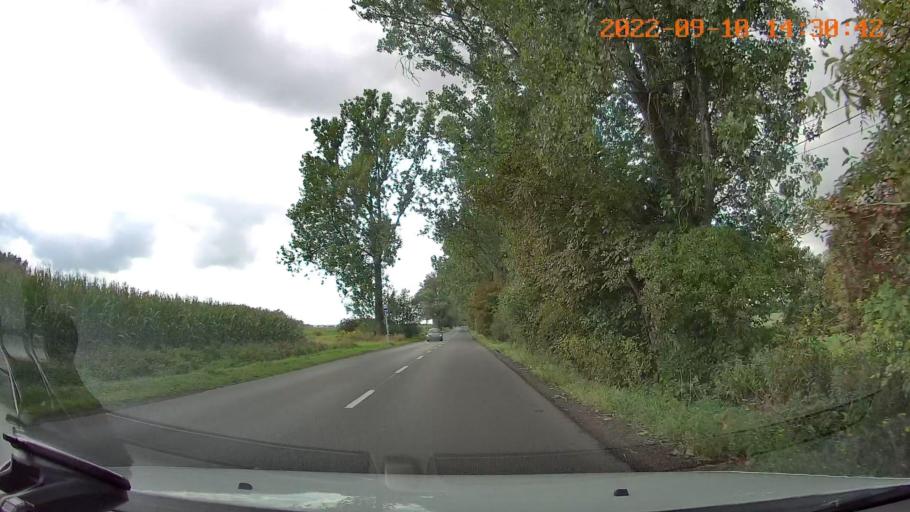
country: PL
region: Lesser Poland Voivodeship
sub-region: Powiat krakowski
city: Kryspinow
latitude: 50.0646
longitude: 19.8192
